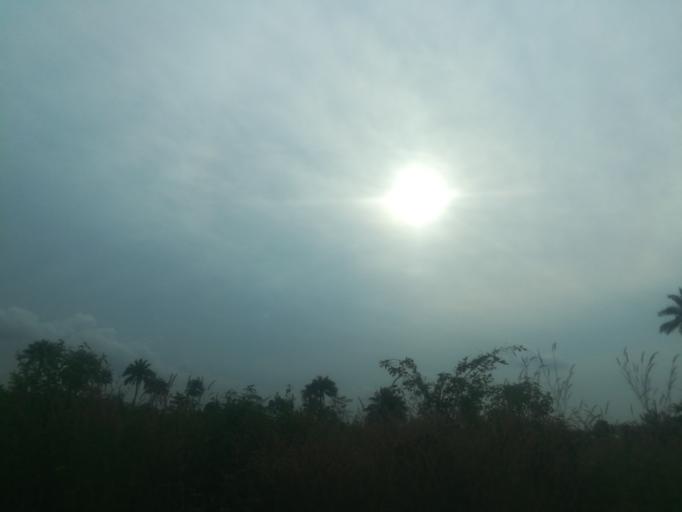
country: NG
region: Ogun
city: Ayetoro
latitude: 7.2503
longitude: 3.1183
